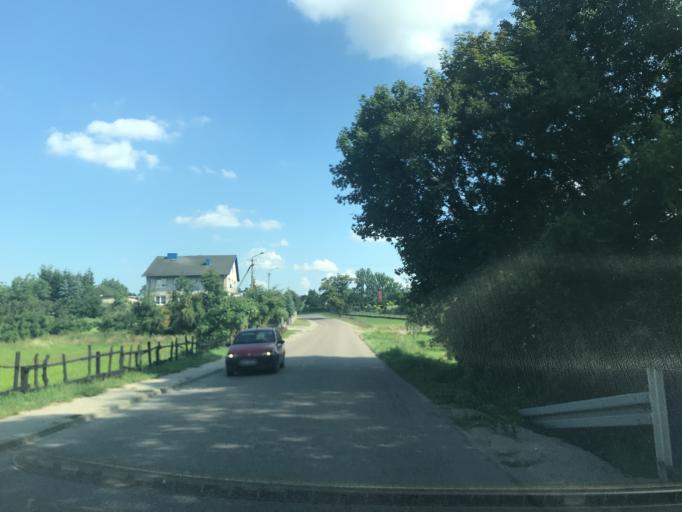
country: PL
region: Masovian Voivodeship
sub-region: Powiat mlawski
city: Mlawa
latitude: 53.1111
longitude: 20.3386
